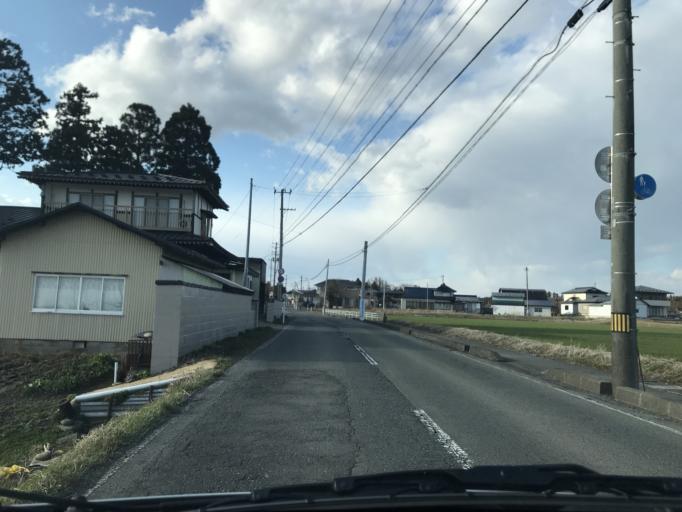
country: JP
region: Iwate
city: Kitakami
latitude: 39.3132
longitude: 141.0691
